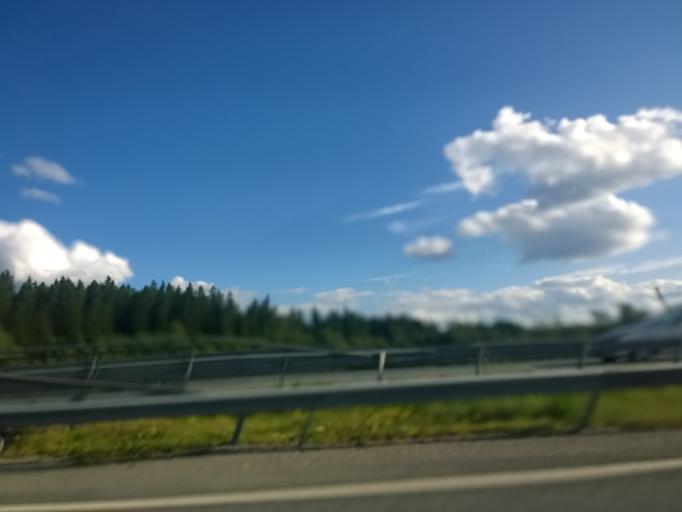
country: FI
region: Pirkanmaa
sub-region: Tampere
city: Tampere
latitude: 61.4602
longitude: 23.7469
